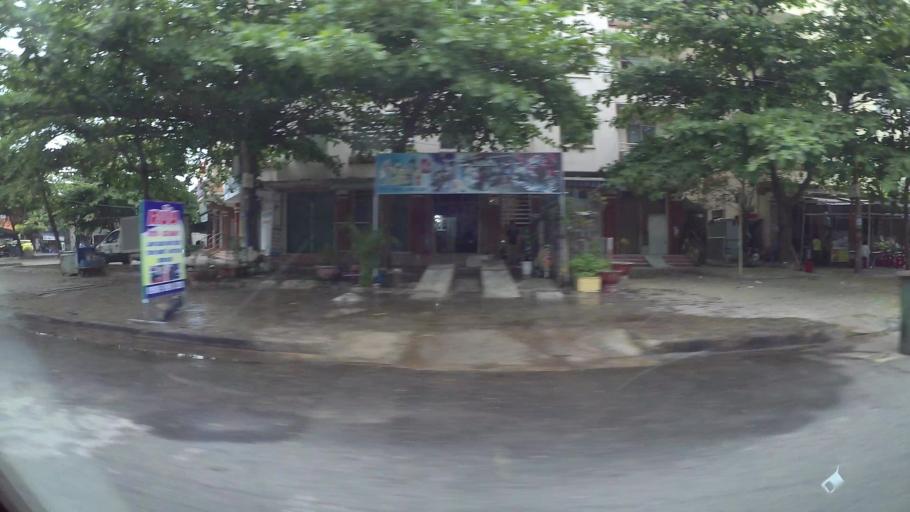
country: VN
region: Da Nang
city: Da Nang
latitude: 16.0895
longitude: 108.2361
